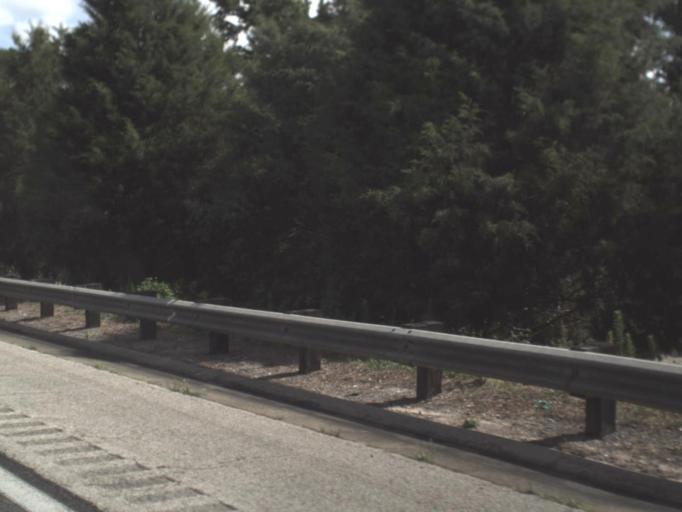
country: US
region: Florida
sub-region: Alachua County
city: Gainesville
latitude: 29.4992
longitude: -82.2956
